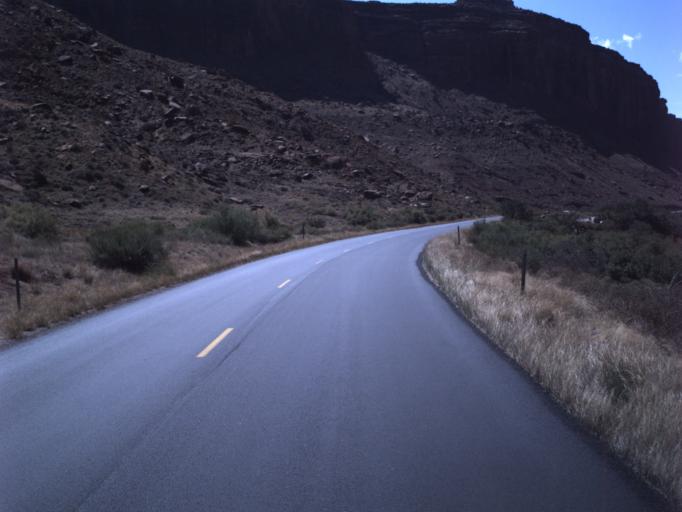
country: US
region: Utah
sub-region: Grand County
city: Moab
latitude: 38.6364
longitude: -109.4806
